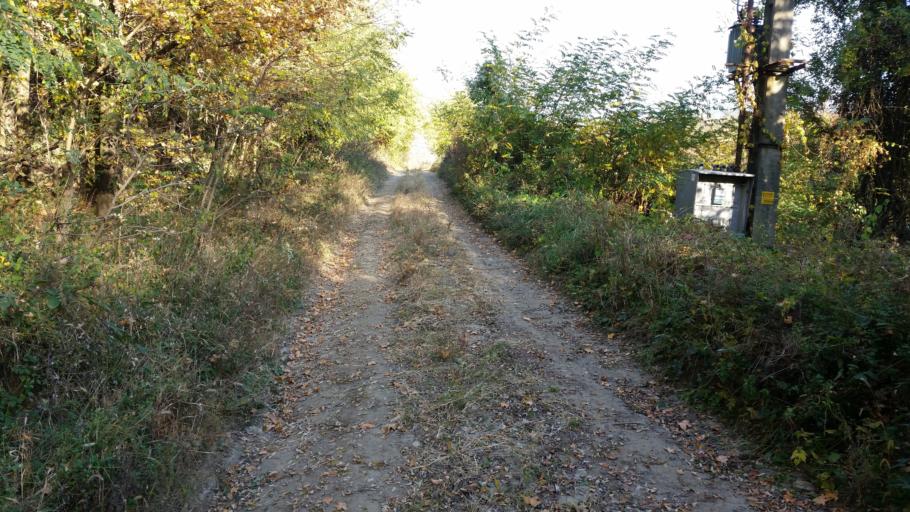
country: SK
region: Nitriansky
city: Sahy
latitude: 48.0405
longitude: 18.9945
